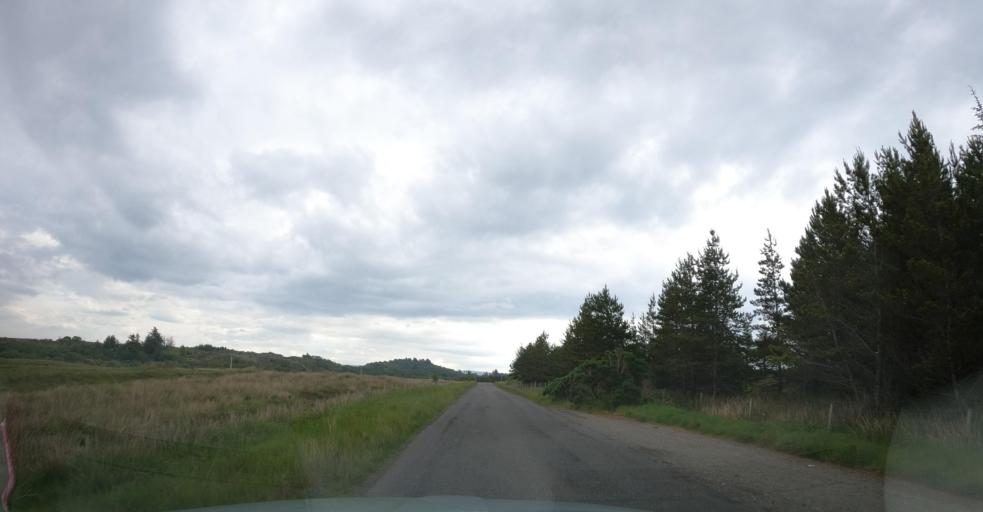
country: GB
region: Scotland
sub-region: Eilean Siar
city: Stornoway
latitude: 58.2031
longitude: -6.4174
